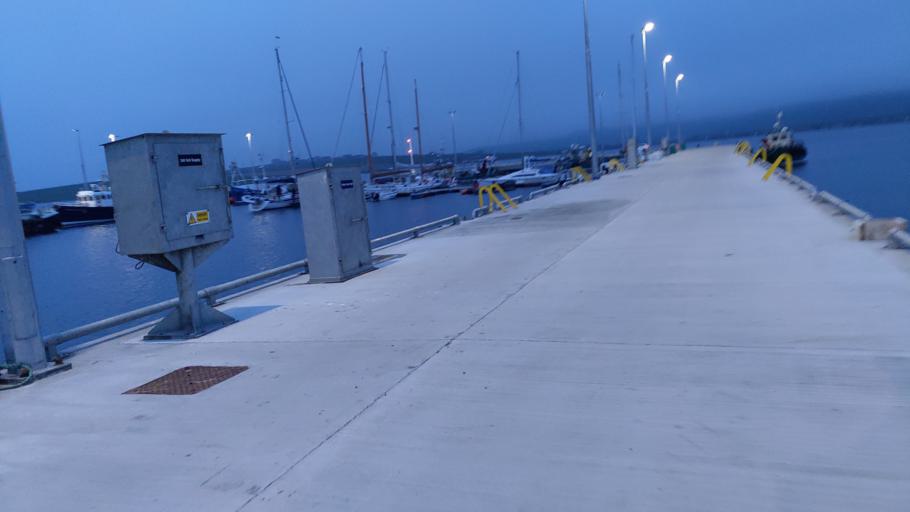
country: GB
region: Scotland
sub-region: Orkney Islands
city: Kirkwall
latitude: 59.3239
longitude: -2.9755
